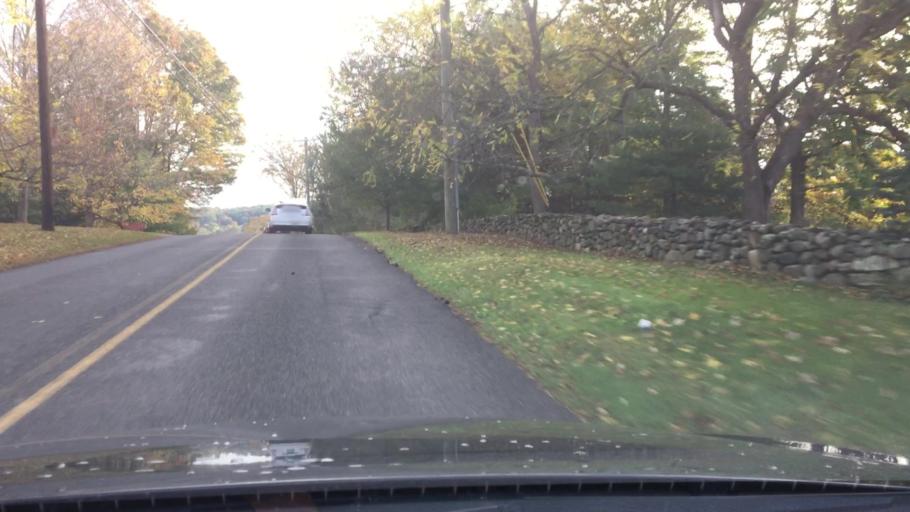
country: US
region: Connecticut
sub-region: Litchfield County
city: New Milford
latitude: 41.5530
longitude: -73.3144
